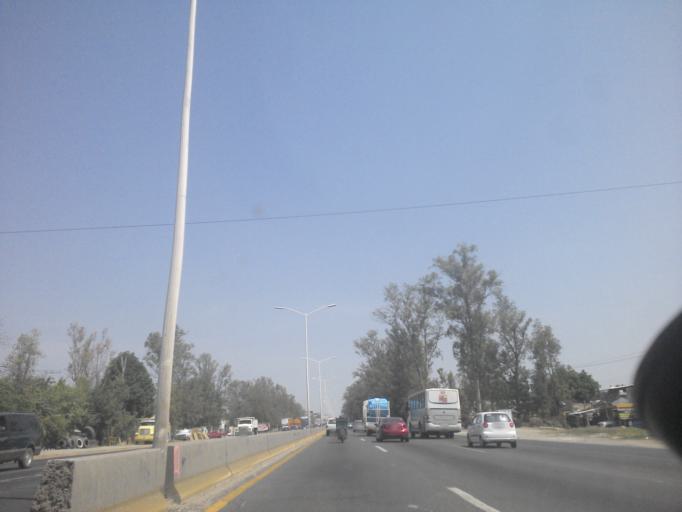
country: MX
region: Jalisco
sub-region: Tlajomulco de Zuniga
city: La Tijera
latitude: 20.6202
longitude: -103.4308
